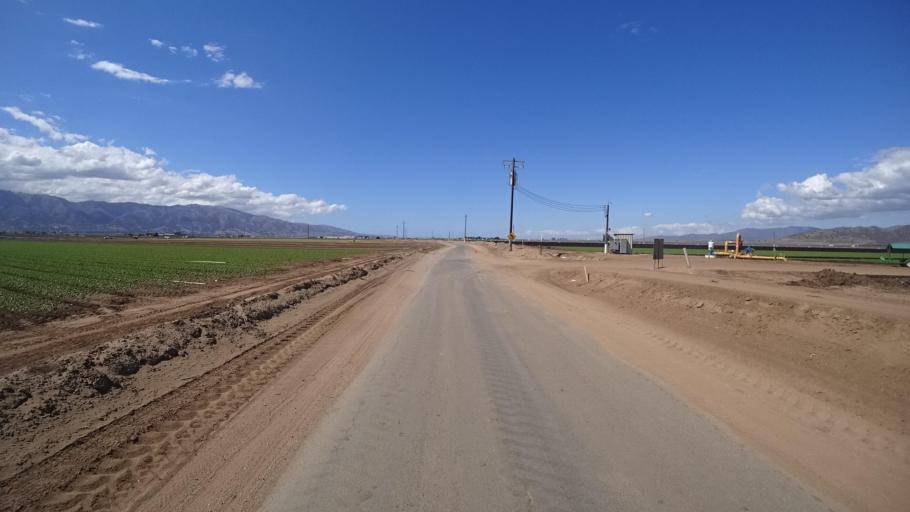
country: US
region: California
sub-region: Monterey County
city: Gonzales
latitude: 36.5301
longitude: -121.4484
